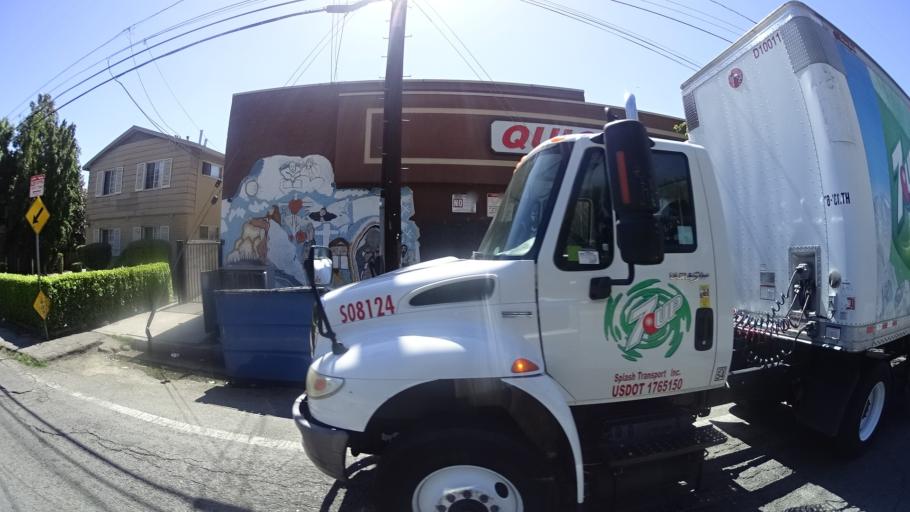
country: US
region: California
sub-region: Los Angeles County
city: Van Nuys
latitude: 34.1935
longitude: -118.4749
